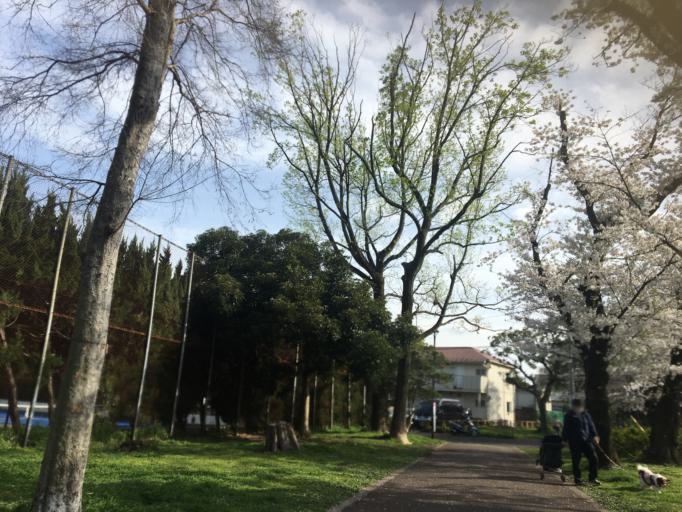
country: JP
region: Tokyo
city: Tokyo
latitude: 35.6937
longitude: 139.6342
